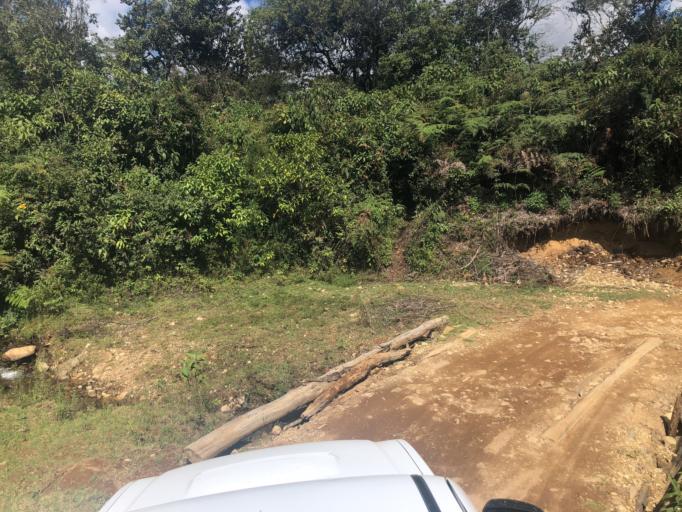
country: CO
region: Cauca
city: Silvia
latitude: 2.6838
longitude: -76.4373
